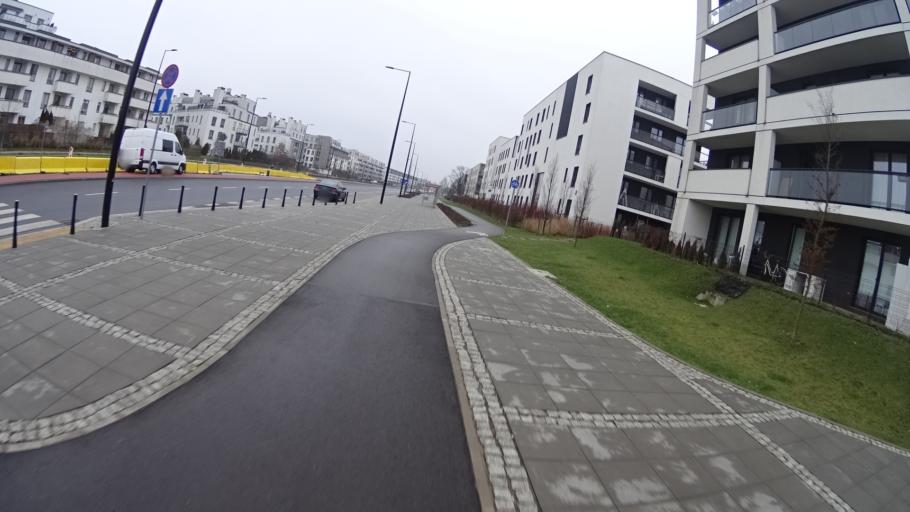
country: PL
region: Masovian Voivodeship
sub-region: Warszawa
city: Wilanow
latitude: 52.1546
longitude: 21.0714
